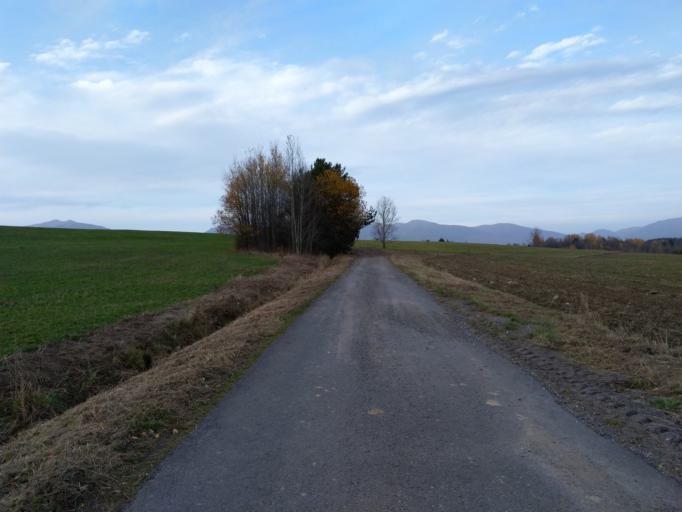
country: SK
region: Zilinsky
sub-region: Okres Liptovsky Mikulas
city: Hybe
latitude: 49.0590
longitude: 19.8261
